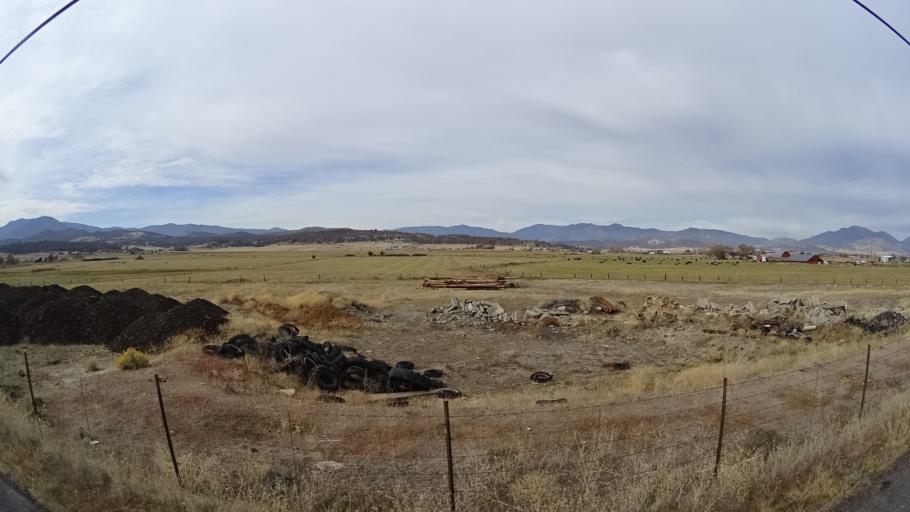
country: US
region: California
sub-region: Siskiyou County
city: Montague
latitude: 41.7030
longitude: -122.5492
